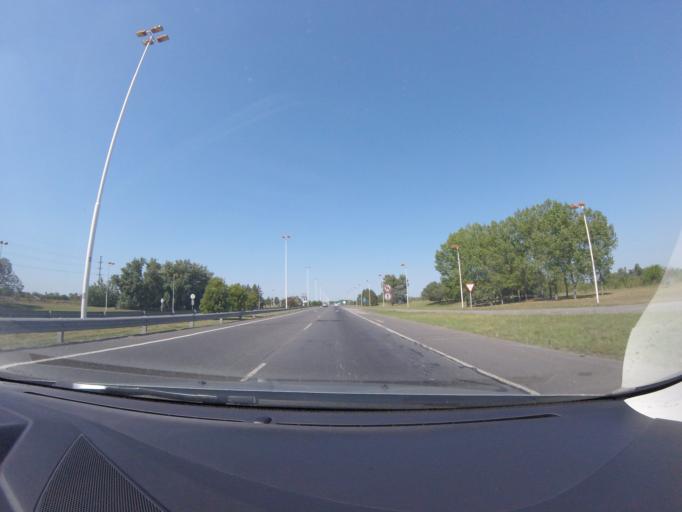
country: AR
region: Buenos Aires
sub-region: Partido de Ezeiza
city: Ezeiza
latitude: -34.9064
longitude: -58.6228
